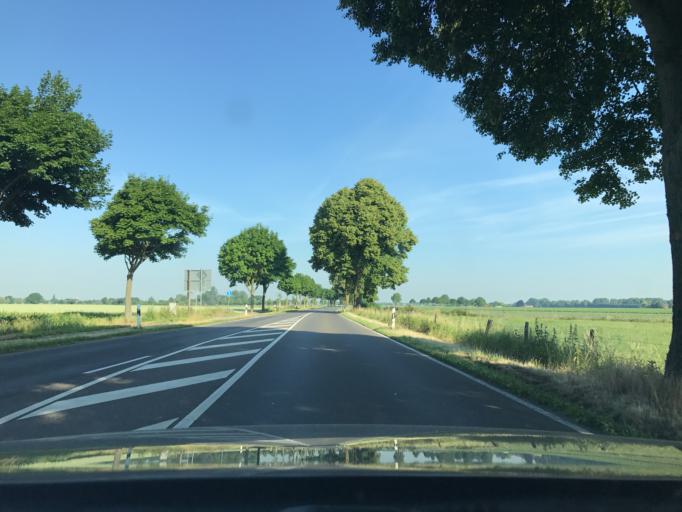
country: DE
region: North Rhine-Westphalia
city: Tonisvorst
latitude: 51.3401
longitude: 6.4635
